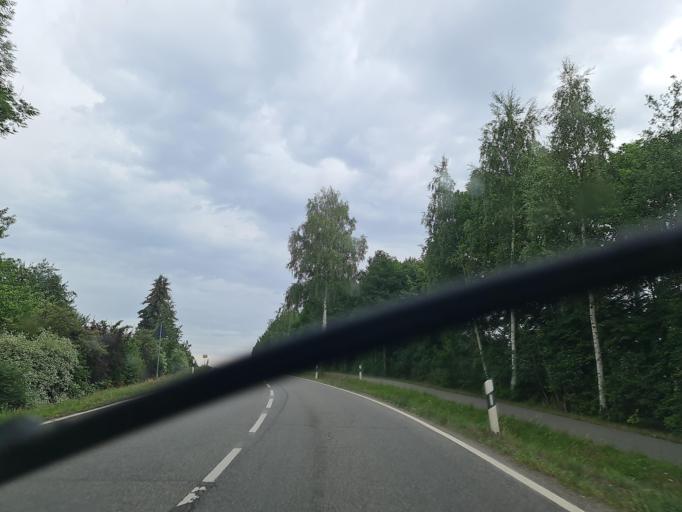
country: DE
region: Saxony
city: Eppendorf
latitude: 50.7915
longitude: 13.2599
